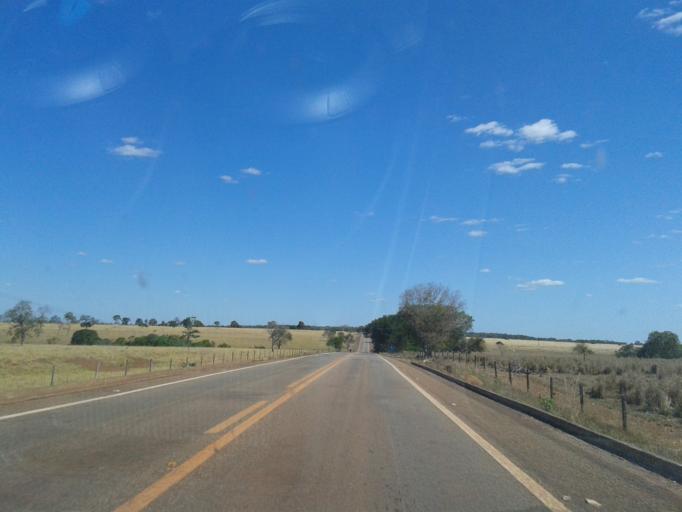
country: BR
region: Goias
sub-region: Sao Miguel Do Araguaia
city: Sao Miguel do Araguaia
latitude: -13.4451
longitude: -50.2920
